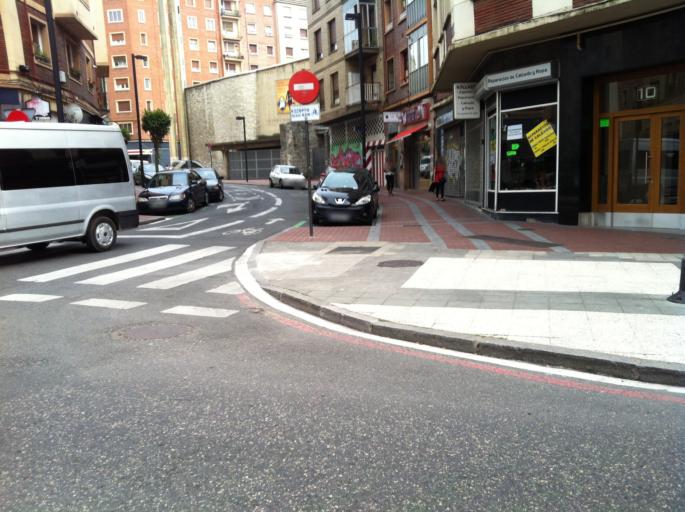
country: ES
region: Basque Country
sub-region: Provincia de Alava
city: Gasteiz / Vitoria
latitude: 42.8526
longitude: -2.6758
